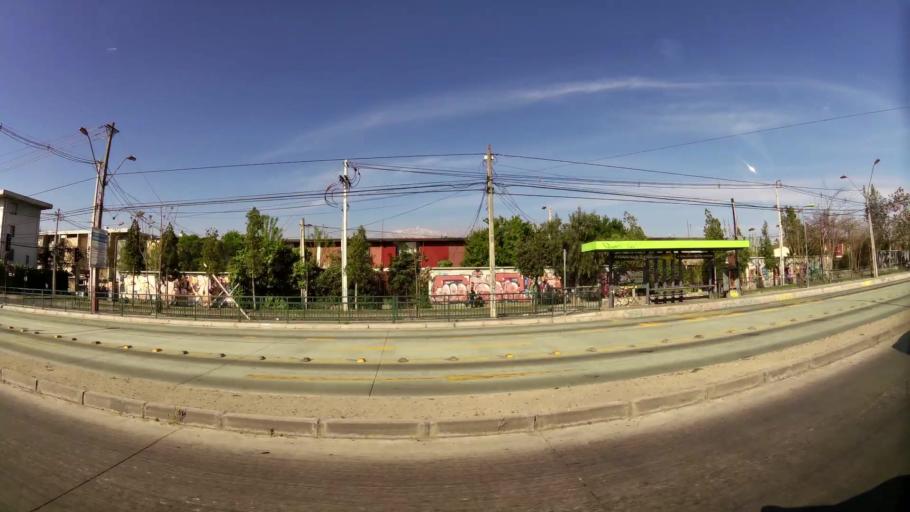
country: CL
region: Santiago Metropolitan
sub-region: Provincia de Santiago
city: Santiago
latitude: -33.4908
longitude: -70.6296
